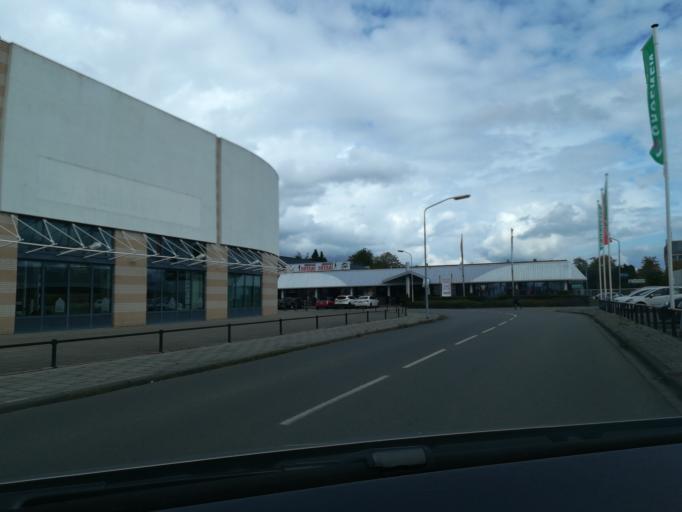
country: NL
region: North Brabant
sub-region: Gemeente Veldhoven
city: Veldhoven
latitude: 51.4134
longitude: 5.4207
